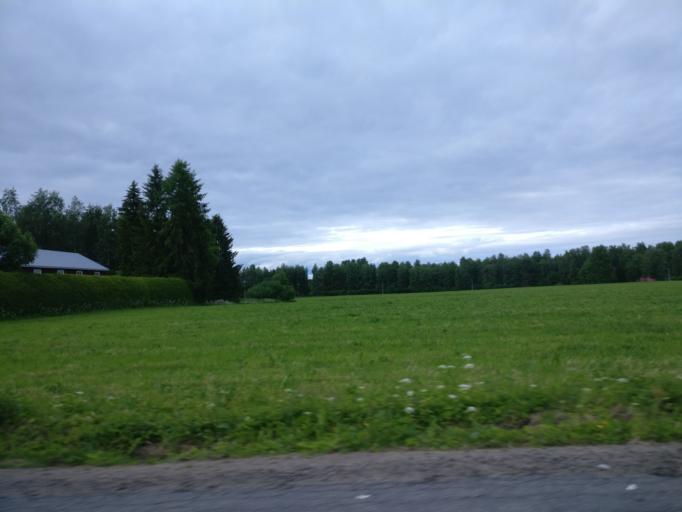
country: FI
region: Southern Savonia
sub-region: Savonlinna
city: Enonkoski
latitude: 61.9767
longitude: 28.9461
